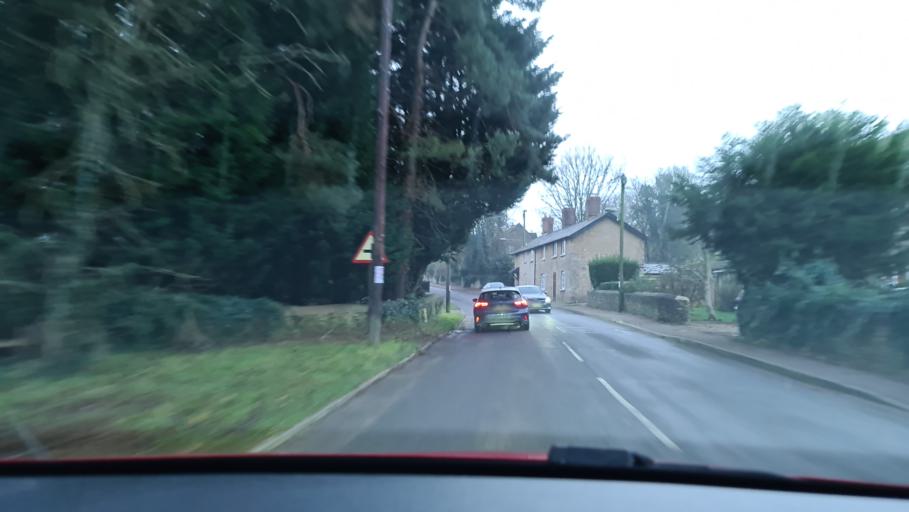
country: GB
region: England
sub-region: Oxfordshire
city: Bicester
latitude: 51.8927
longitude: -1.1896
